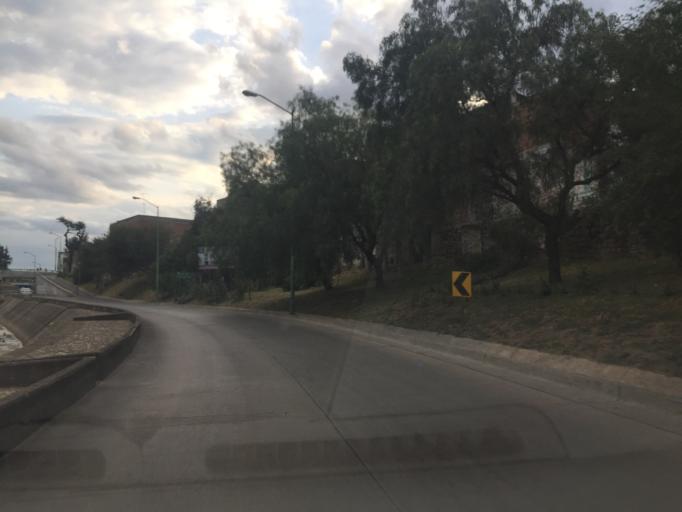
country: MX
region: Guanajuato
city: Leon
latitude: 21.1439
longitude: -101.6802
